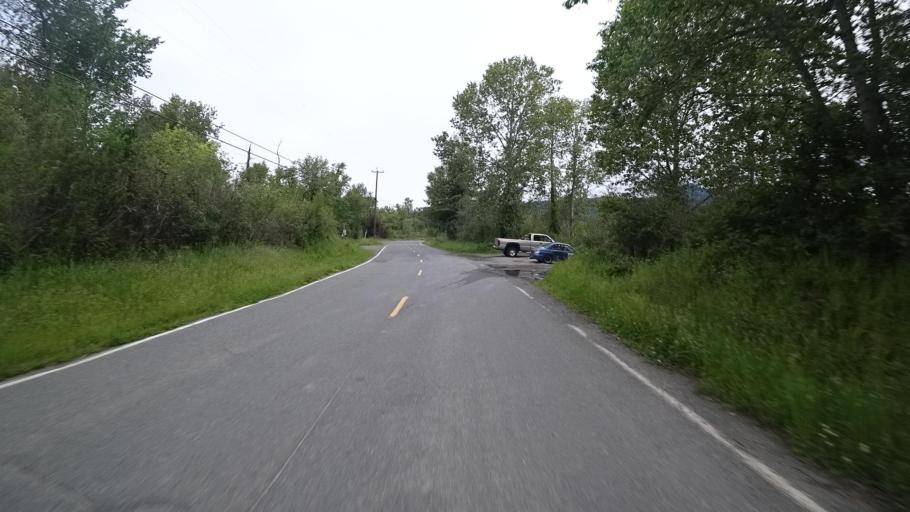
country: US
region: California
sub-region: Humboldt County
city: Blue Lake
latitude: 40.8726
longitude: -123.9935
